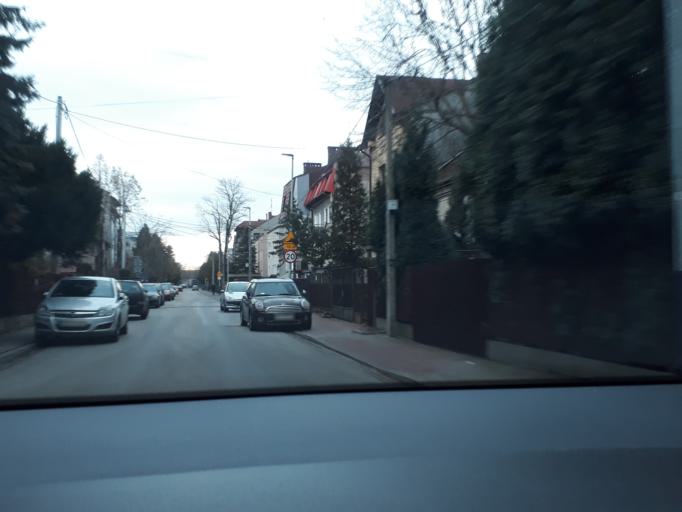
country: PL
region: Lesser Poland Voivodeship
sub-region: Krakow
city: Krakow
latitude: 50.0781
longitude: 19.9721
